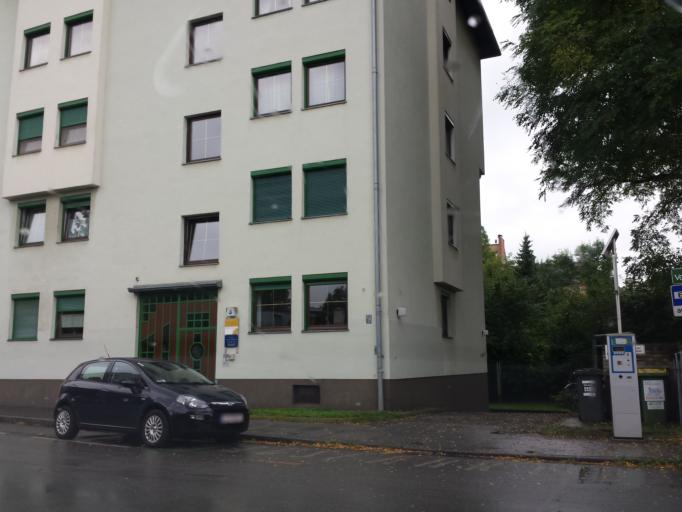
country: AT
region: Styria
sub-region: Graz Stadt
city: Graz
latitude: 47.0840
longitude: 15.4341
